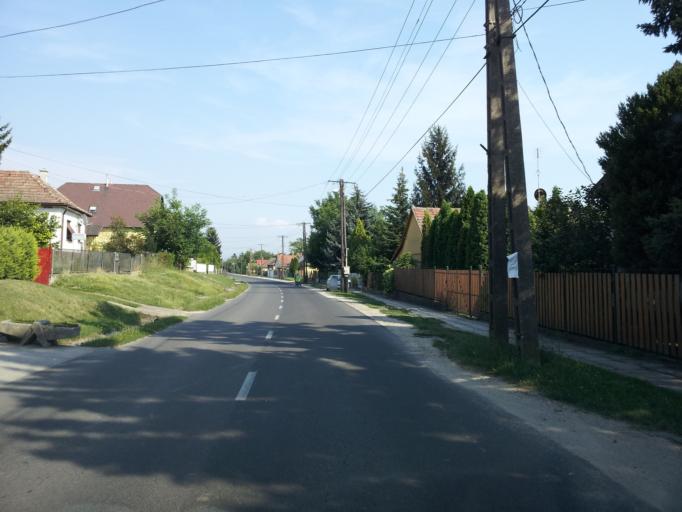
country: HU
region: Veszprem
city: Balatonkenese
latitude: 47.0421
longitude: 18.0994
